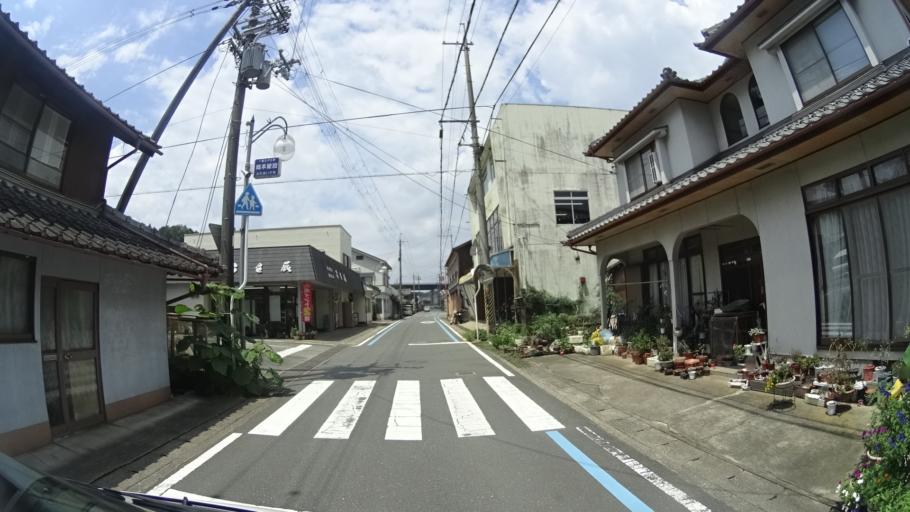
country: JP
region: Kyoto
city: Ayabe
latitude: 35.1782
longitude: 135.3719
